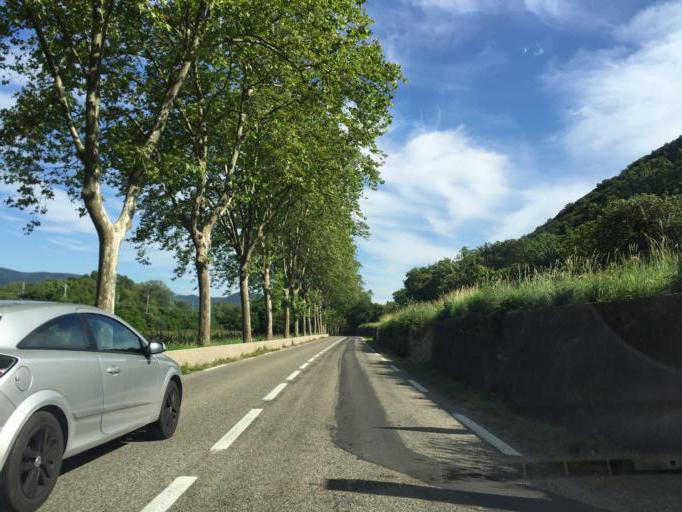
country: FR
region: Rhone-Alpes
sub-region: Departement de la Drome
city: Saulce-sur-Rhone
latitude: 44.7017
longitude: 4.7658
